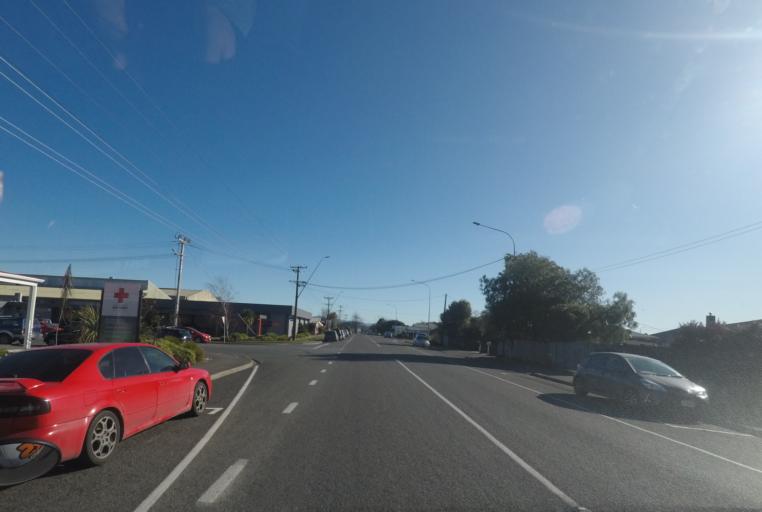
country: NZ
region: Nelson
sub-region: Nelson City
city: Nelson
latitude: -41.2899
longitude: 173.2414
